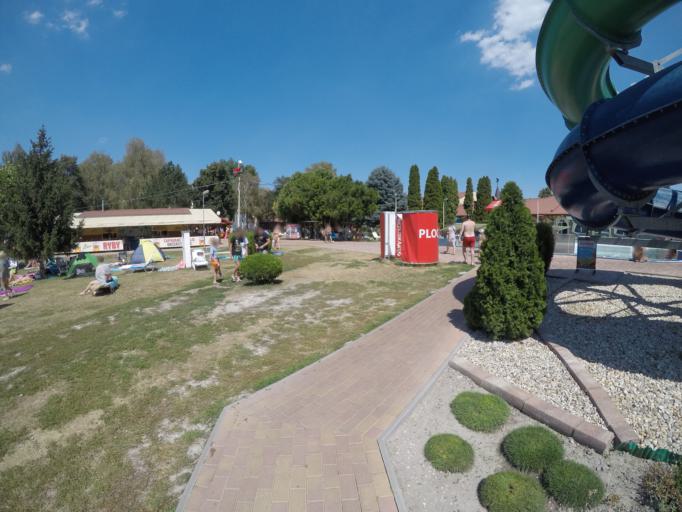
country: SK
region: Trnavsky
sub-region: Okres Dunajska Streda
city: Velky Meder
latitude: 47.8460
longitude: 17.7602
